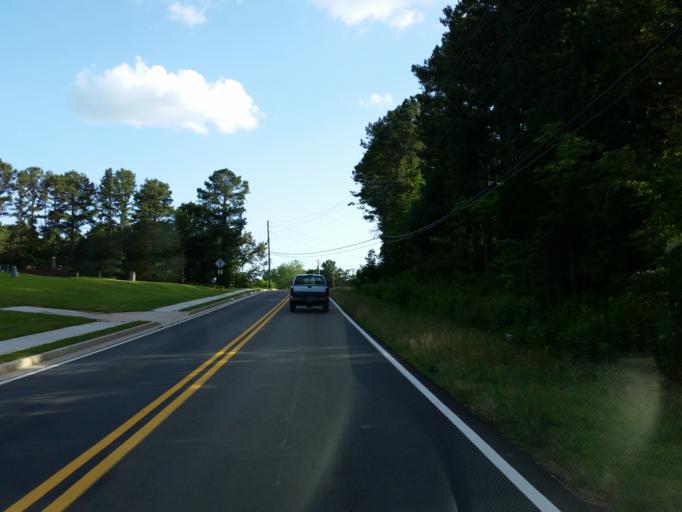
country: US
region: Georgia
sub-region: Cherokee County
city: Woodstock
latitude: 34.0688
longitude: -84.5503
